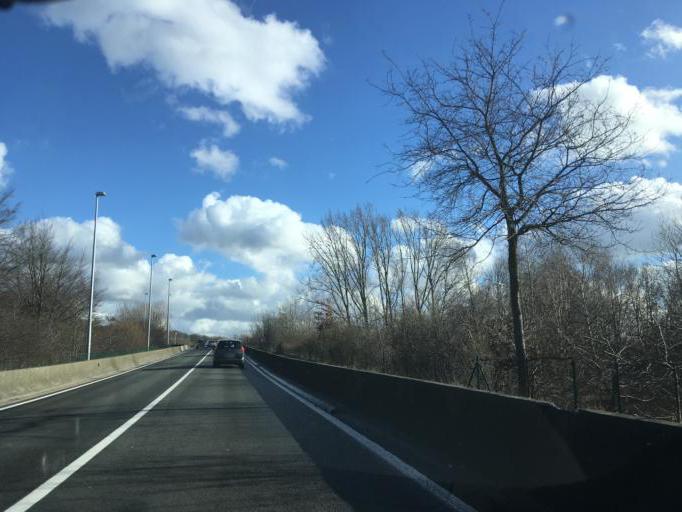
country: BE
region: Flanders
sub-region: Provincie Oost-Vlaanderen
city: Merelbeke
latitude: 51.0016
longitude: 3.7662
